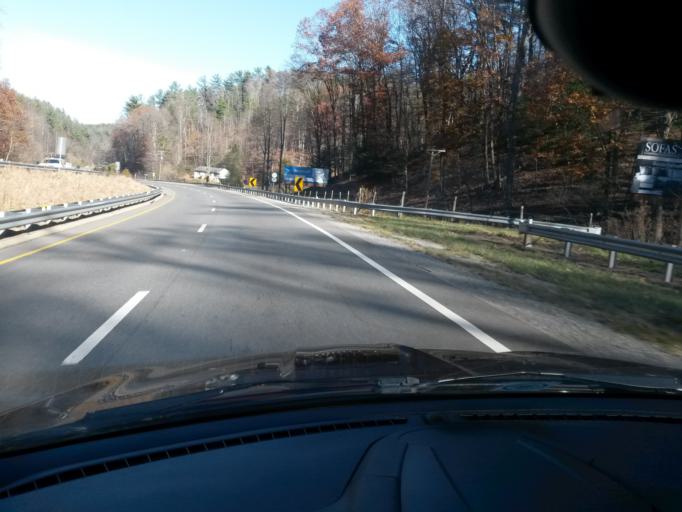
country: US
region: Virginia
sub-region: Roanoke County
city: Narrows
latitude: 37.1621
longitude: -79.9471
